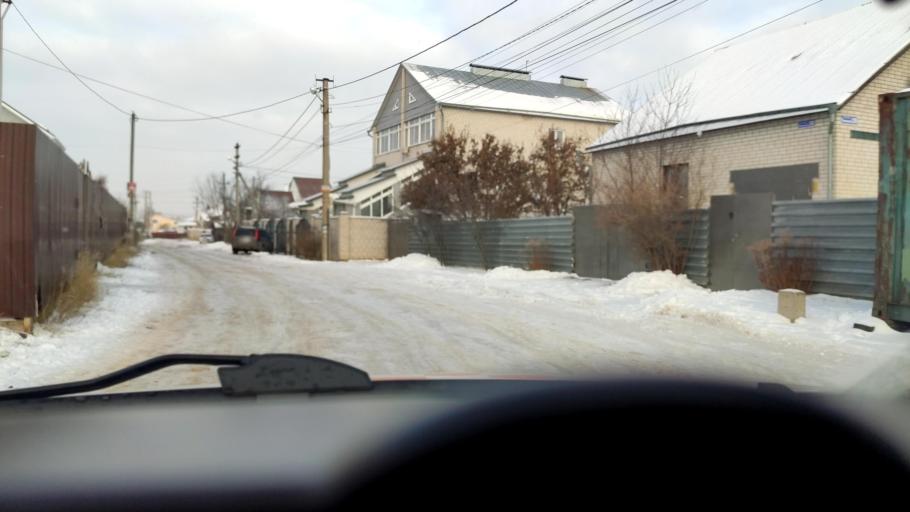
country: RU
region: Voronezj
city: Podgornoye
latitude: 51.7267
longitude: 39.1612
